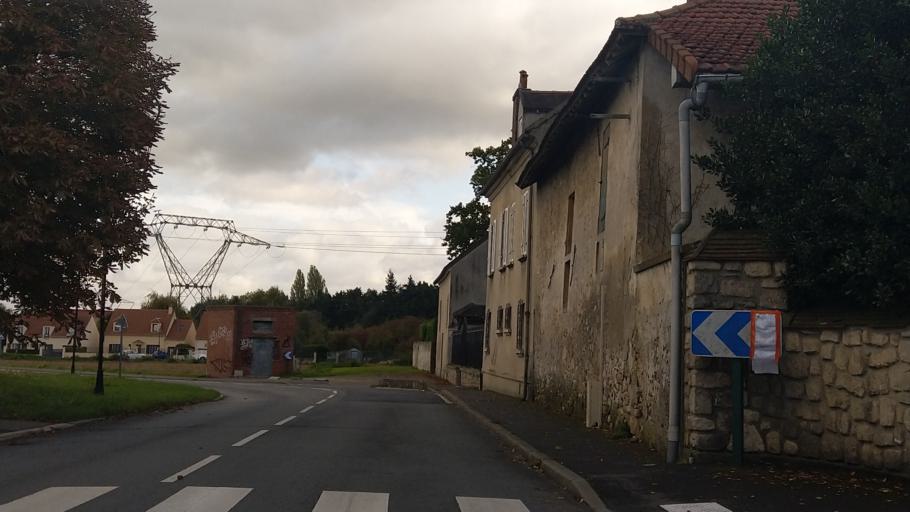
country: FR
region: Ile-de-France
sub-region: Departement du Val-d'Oise
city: Baillet-en-France
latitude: 49.0576
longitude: 2.2910
